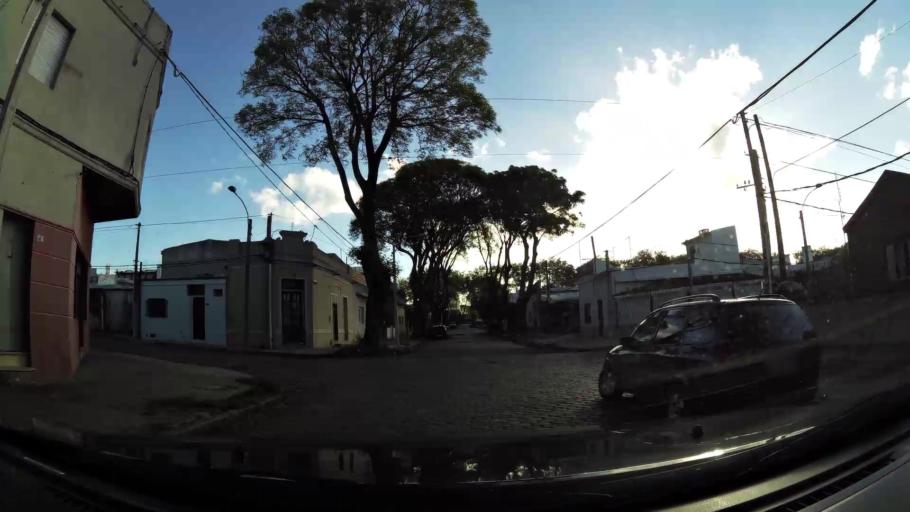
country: UY
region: Montevideo
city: Montevideo
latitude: -34.8842
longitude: -56.1309
